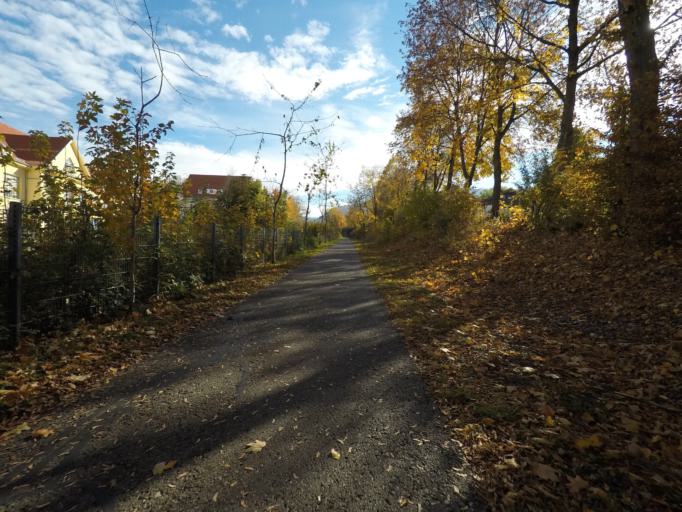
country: DE
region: Baden-Wuerttemberg
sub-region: Tuebingen Region
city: Pfullingen
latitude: 48.4533
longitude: 9.2315
